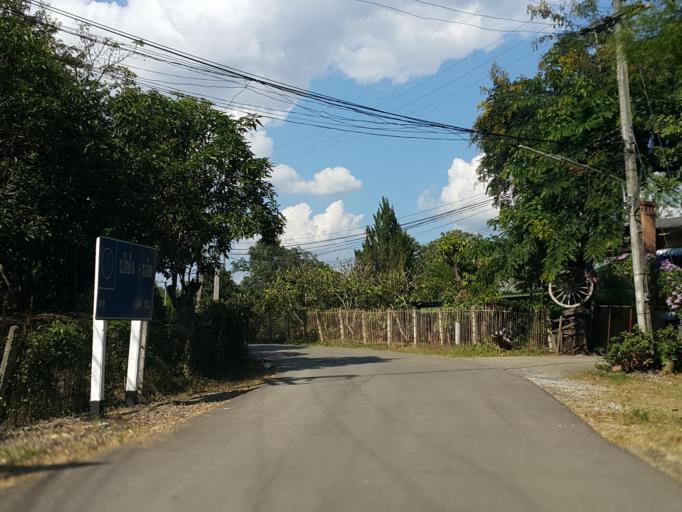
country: TH
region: Chiang Mai
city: San Sai
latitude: 18.9318
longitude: 98.9191
